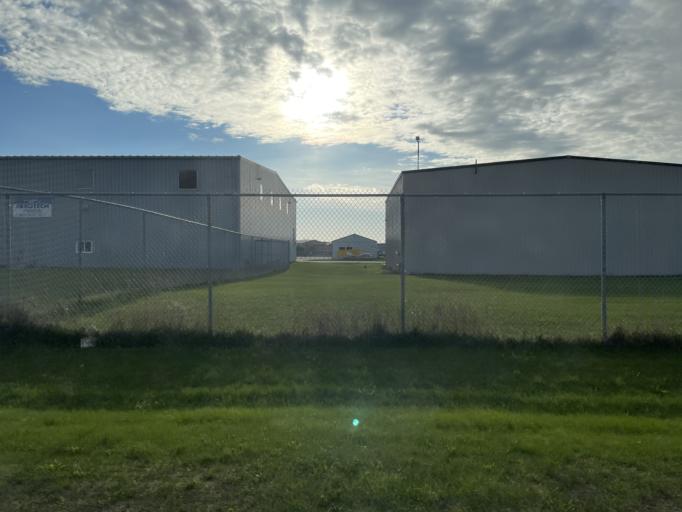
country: CA
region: Ontario
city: Cambridge
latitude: 43.4526
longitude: -80.3813
